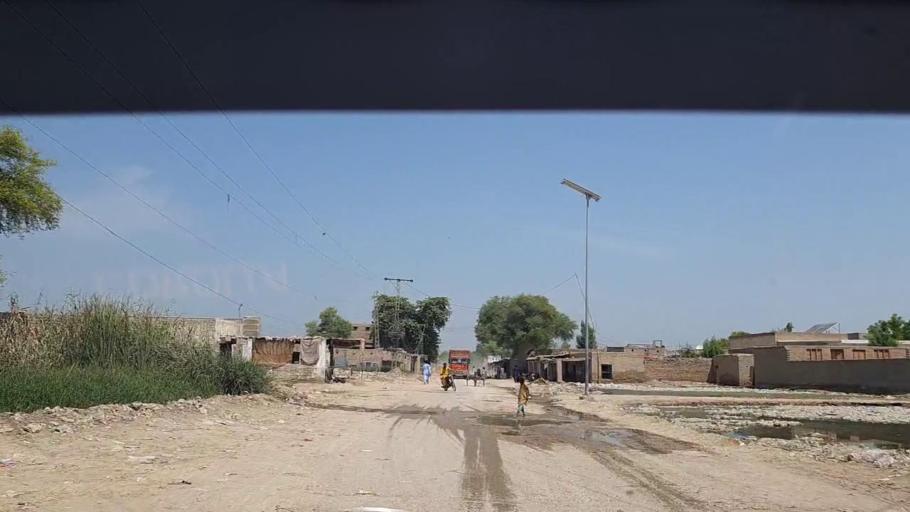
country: PK
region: Sindh
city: Rustam jo Goth
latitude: 28.0801
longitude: 68.7856
